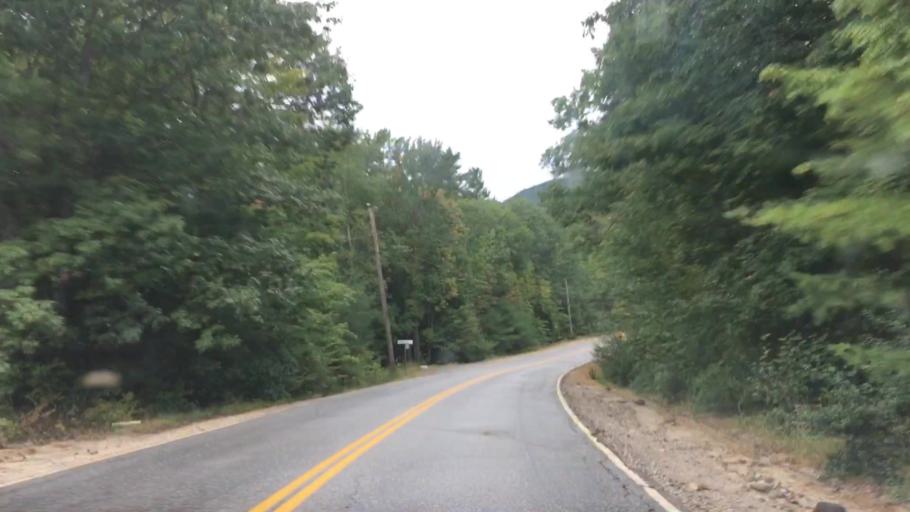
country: US
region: Maine
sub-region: Cumberland County
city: Raymond
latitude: 43.9453
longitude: -70.4609
